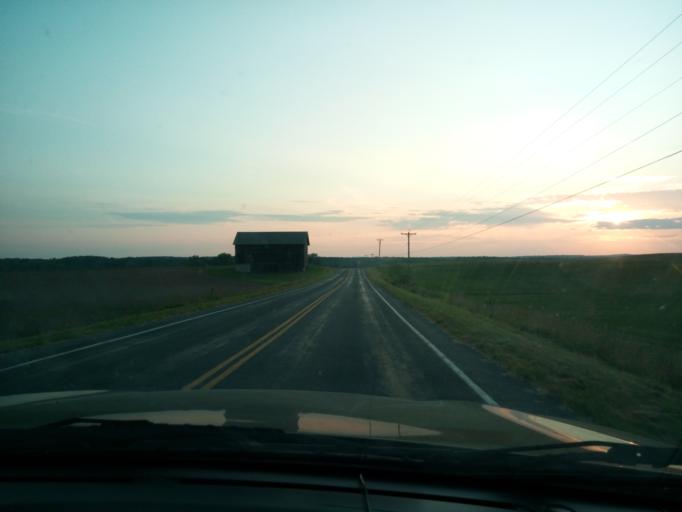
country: US
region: New York
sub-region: Seneca County
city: Bridgeport
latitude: 43.0219
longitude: -76.7765
